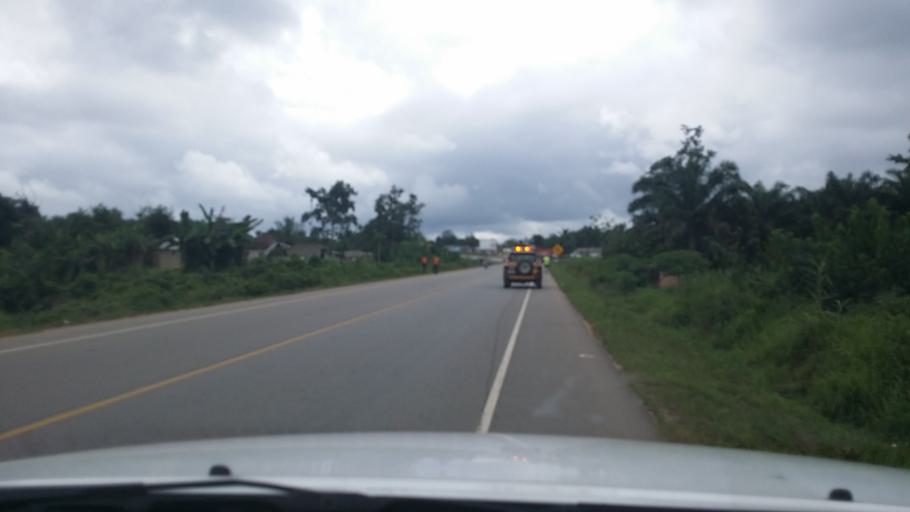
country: LR
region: Bong
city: Gbarnga
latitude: 7.0025
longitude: -9.2936
